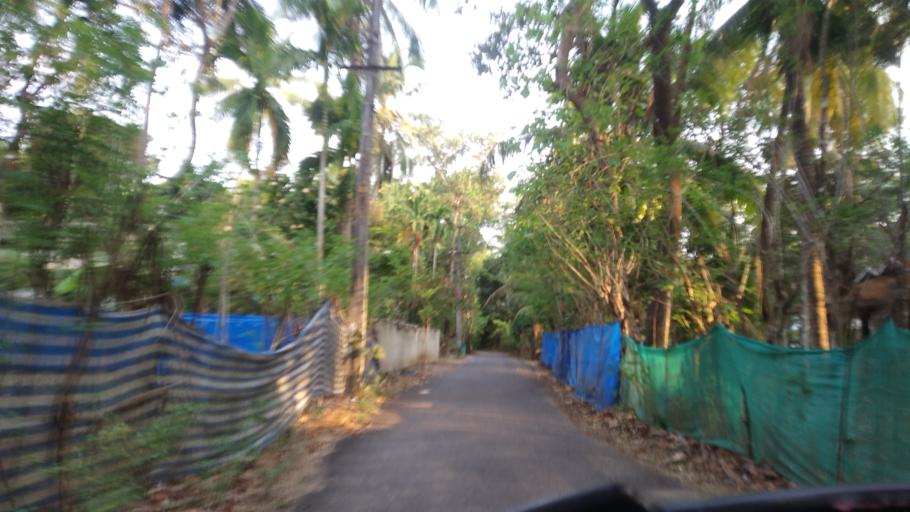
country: IN
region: Kerala
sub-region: Thrissur District
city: Thanniyam
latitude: 10.4126
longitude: 76.0880
